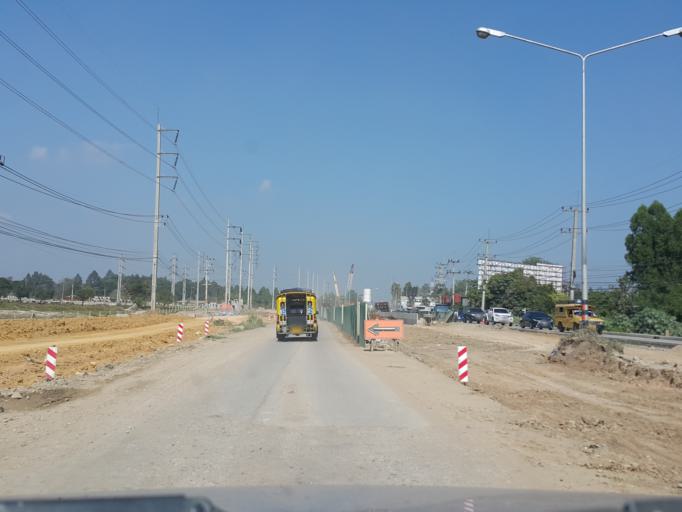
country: TH
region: Chiang Mai
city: Chiang Mai
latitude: 18.8648
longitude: 98.9648
